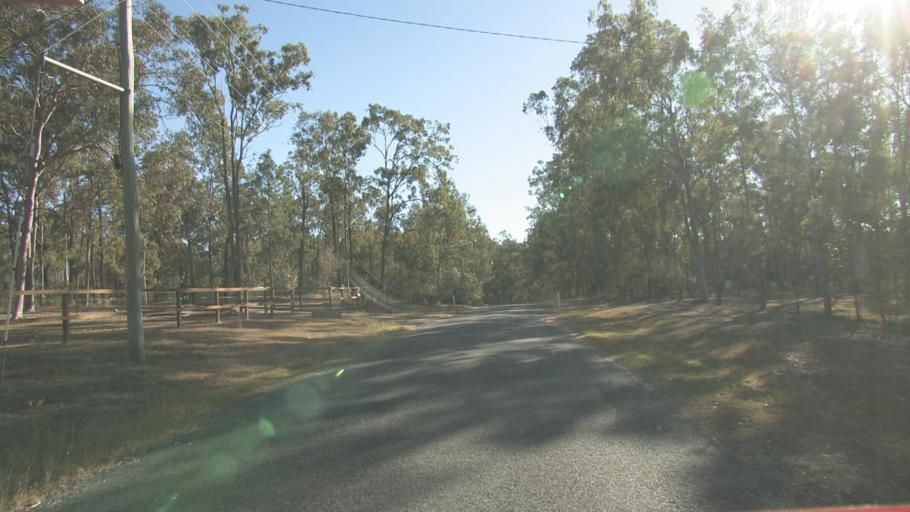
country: AU
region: Queensland
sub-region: Logan
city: North Maclean
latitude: -27.7814
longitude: 152.9652
